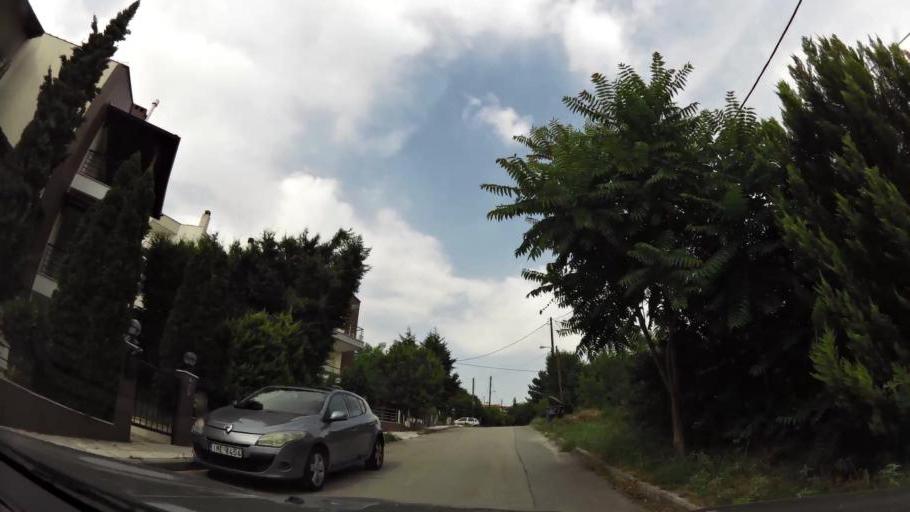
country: GR
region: Central Macedonia
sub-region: Nomos Thessalonikis
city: Oraiokastro
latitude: 40.7132
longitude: 22.9231
